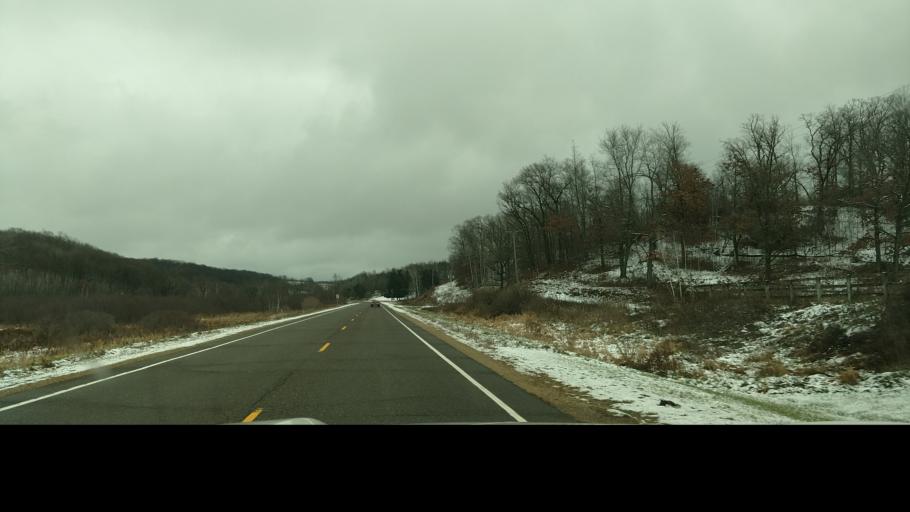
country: US
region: Wisconsin
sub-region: Dunn County
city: Tainter Lake
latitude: 45.1274
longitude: -91.8453
